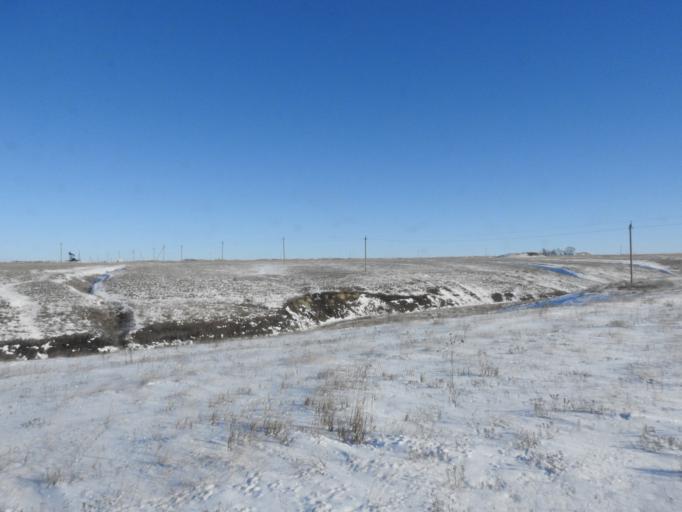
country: RU
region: Saratov
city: Lysyye Gory
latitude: 51.4540
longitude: 44.9618
